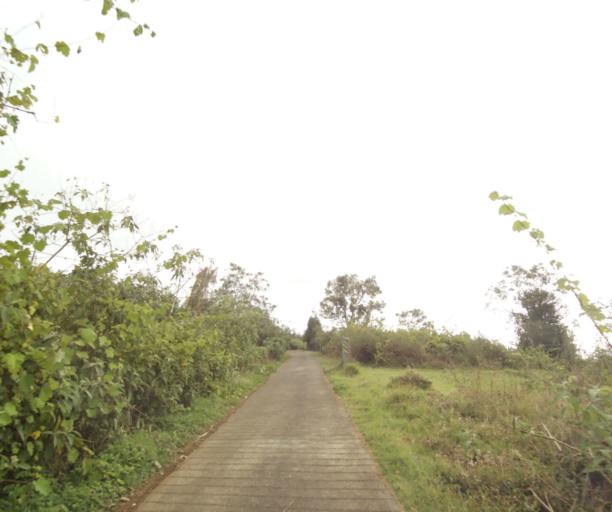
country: RE
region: Reunion
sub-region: Reunion
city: Saint-Paul
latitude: -21.0131
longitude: 55.3528
